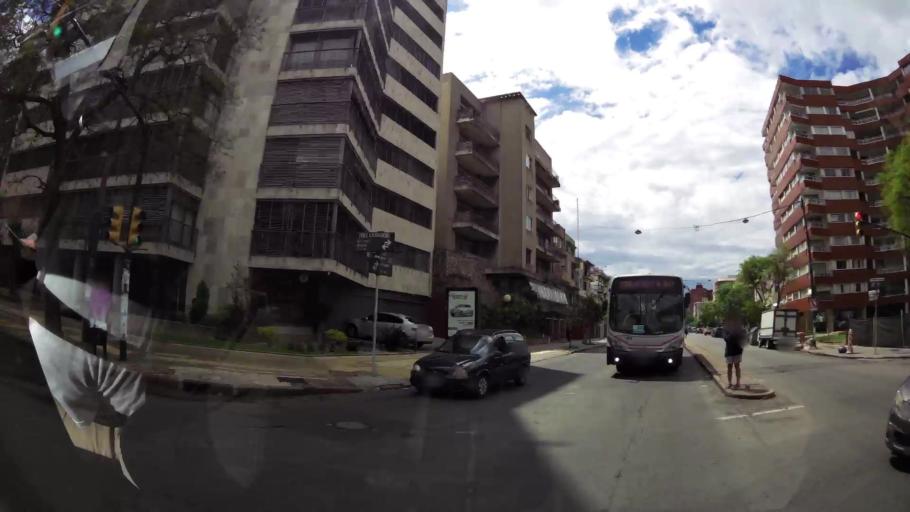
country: UY
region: Montevideo
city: Montevideo
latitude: -34.9110
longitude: -56.1631
